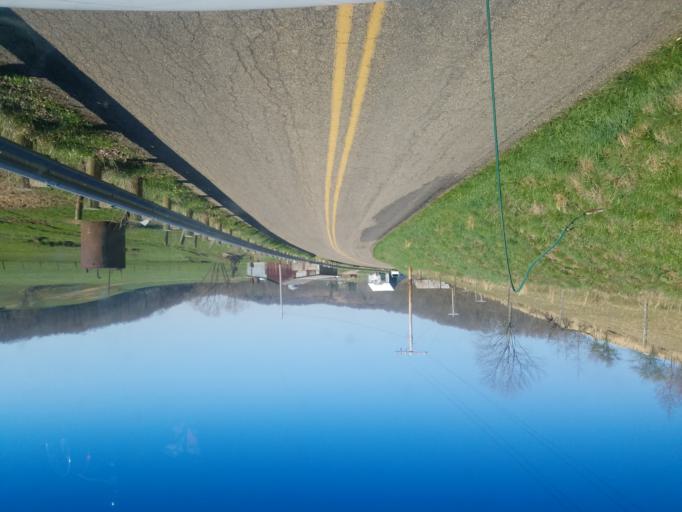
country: US
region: Ohio
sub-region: Muskingum County
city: Frazeysburg
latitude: 40.2464
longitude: -82.2043
